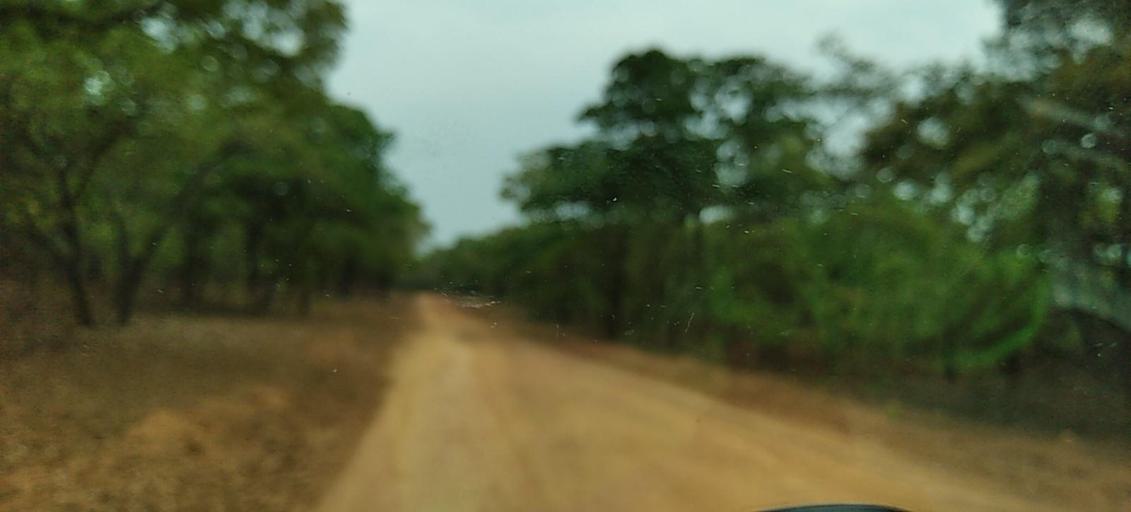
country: ZM
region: North-Western
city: Solwezi
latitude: -12.9185
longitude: 26.5597
